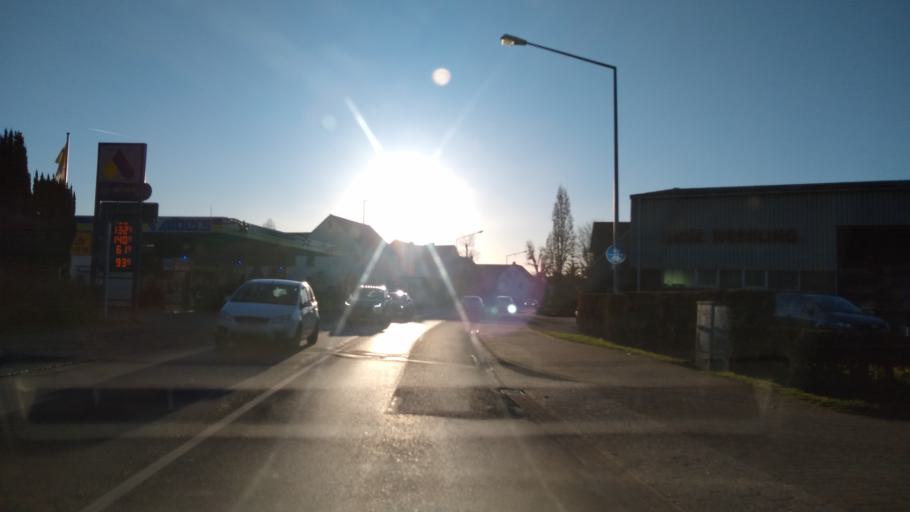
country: DE
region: Lower Saxony
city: Cloppenburg
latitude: 52.8509
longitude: 8.0514
